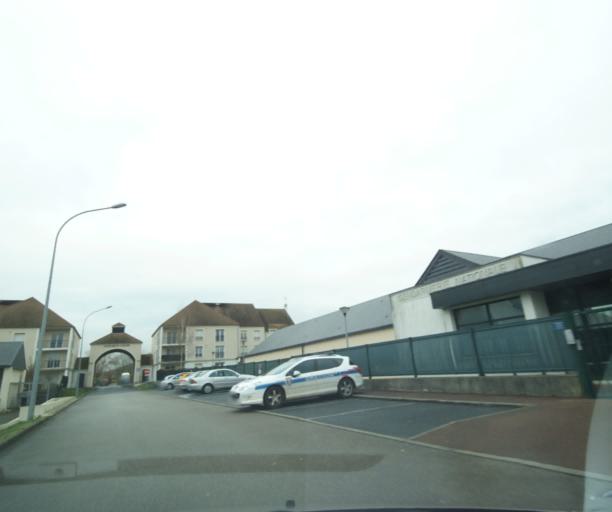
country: FR
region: Picardie
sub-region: Departement de l'Oise
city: Noyon
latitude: 49.5754
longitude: 2.9886
